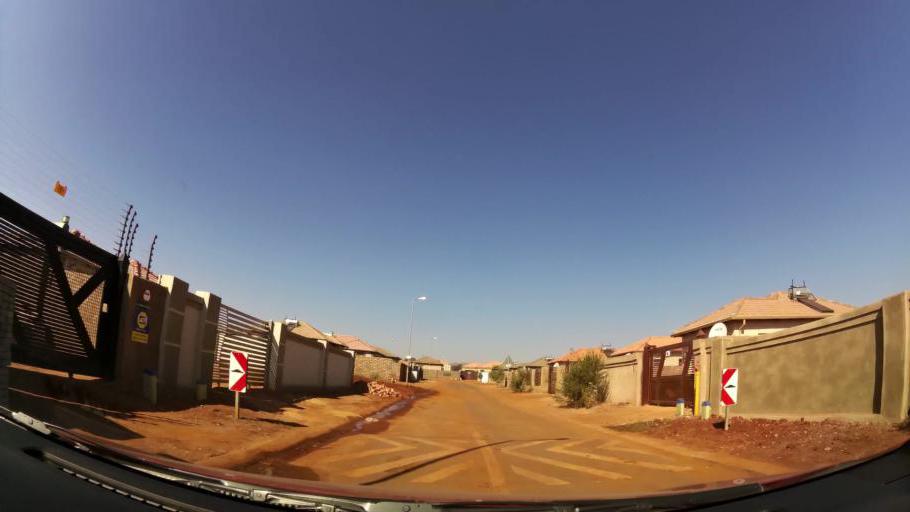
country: ZA
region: North-West
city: Ga-Rankuwa
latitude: -25.6382
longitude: 28.0738
